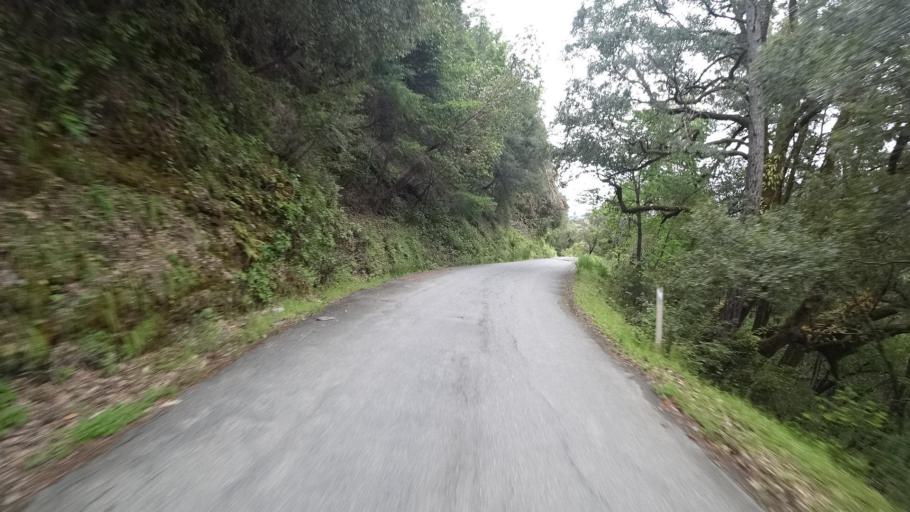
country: US
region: California
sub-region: Humboldt County
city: Willow Creek
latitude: 40.9356
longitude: -123.6158
